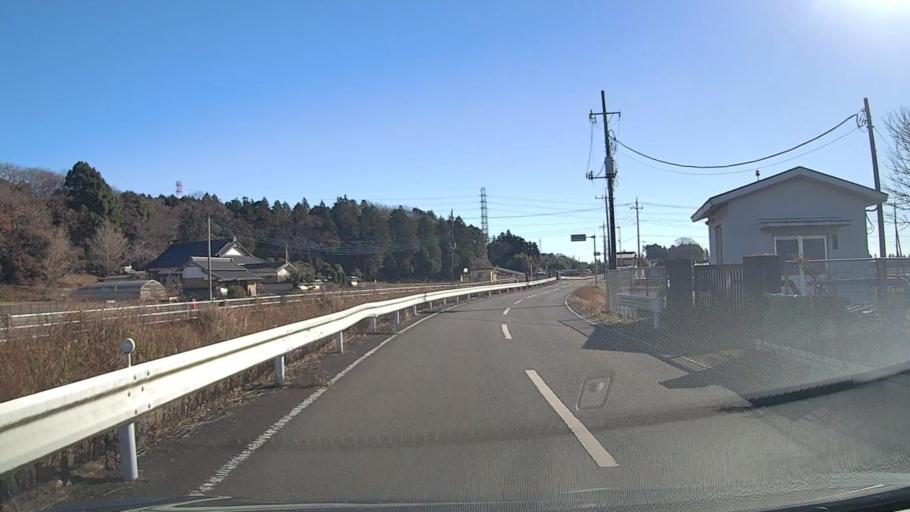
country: JP
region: Ibaraki
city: Mito-shi
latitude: 36.4353
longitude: 140.4415
